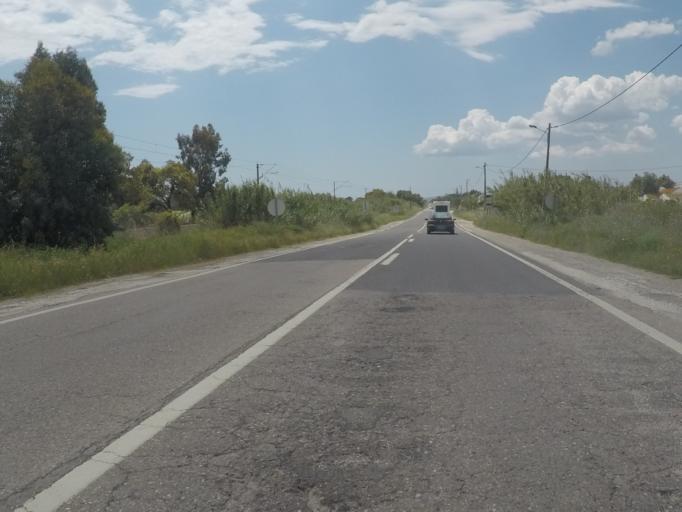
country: PT
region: Setubal
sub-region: Setubal
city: Setubal
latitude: 38.5599
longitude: -8.7893
